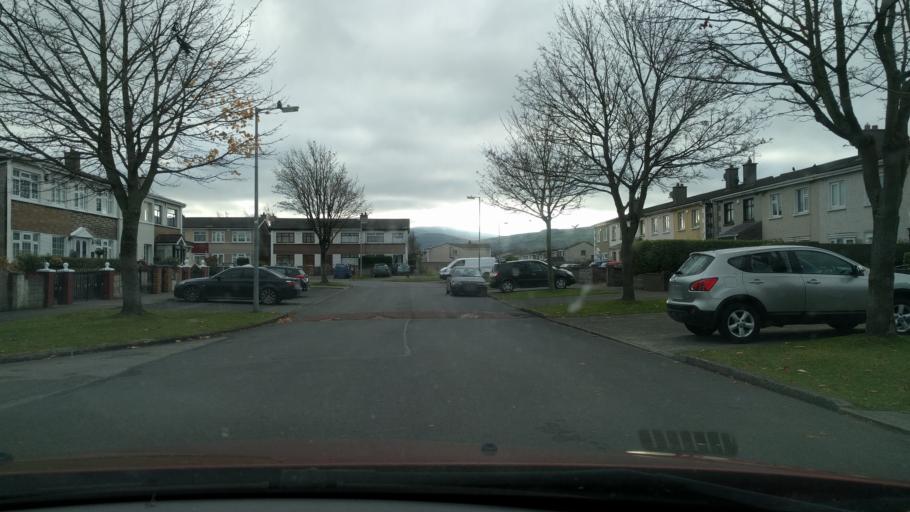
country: IE
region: Leinster
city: Tallaght
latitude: 53.2909
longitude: -6.3847
